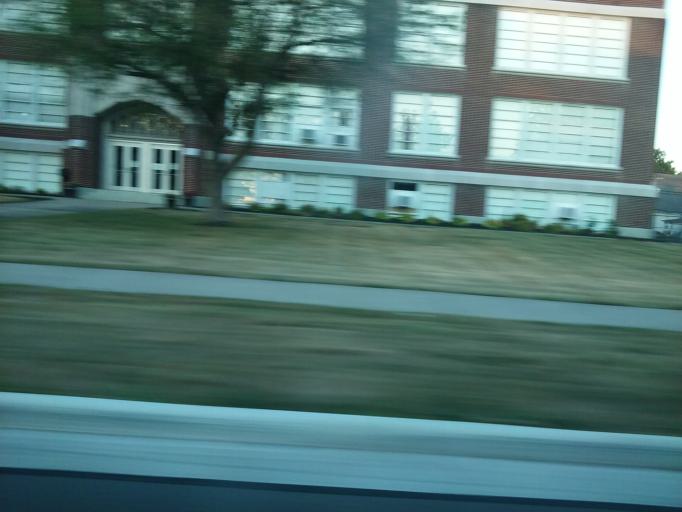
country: US
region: Ohio
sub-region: Hancock County
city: Findlay
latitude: 41.0491
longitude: -83.6500
